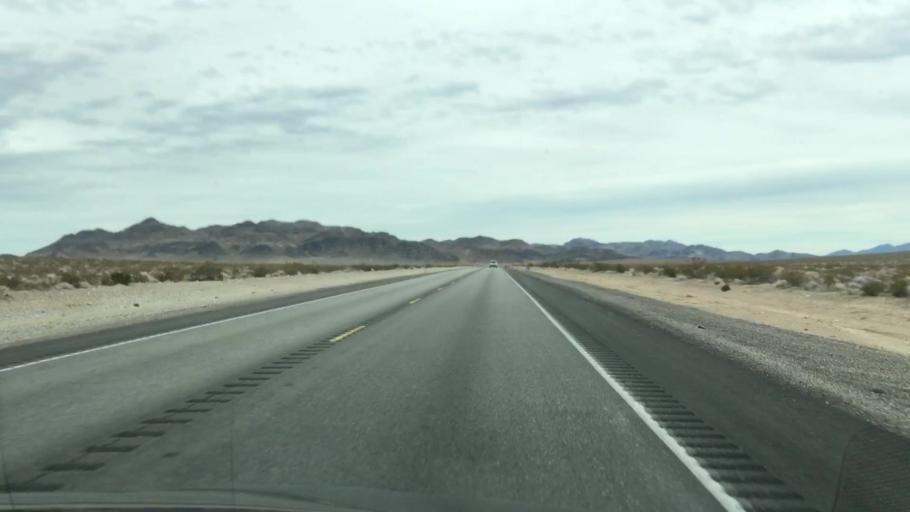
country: US
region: Nevada
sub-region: Nye County
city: Beatty
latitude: 36.6316
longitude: -116.3395
